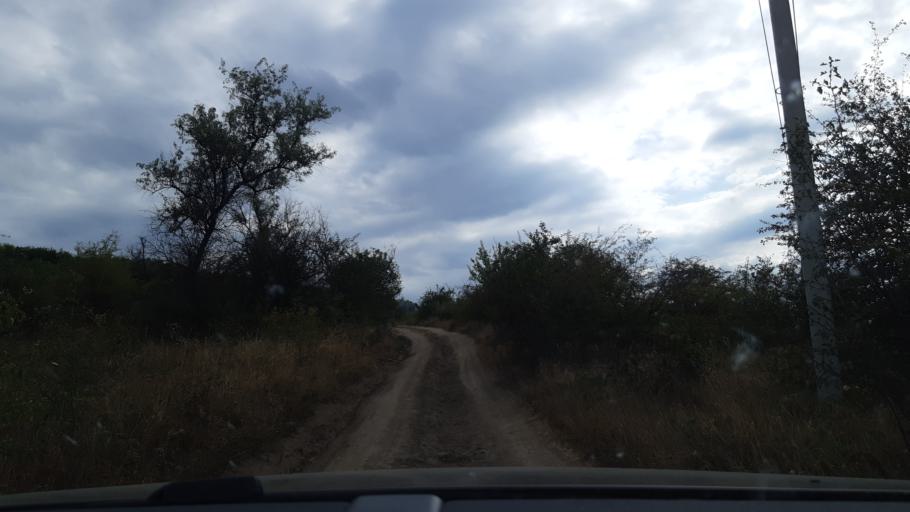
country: MD
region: Chisinau
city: Vatra
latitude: 47.0605
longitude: 28.7389
